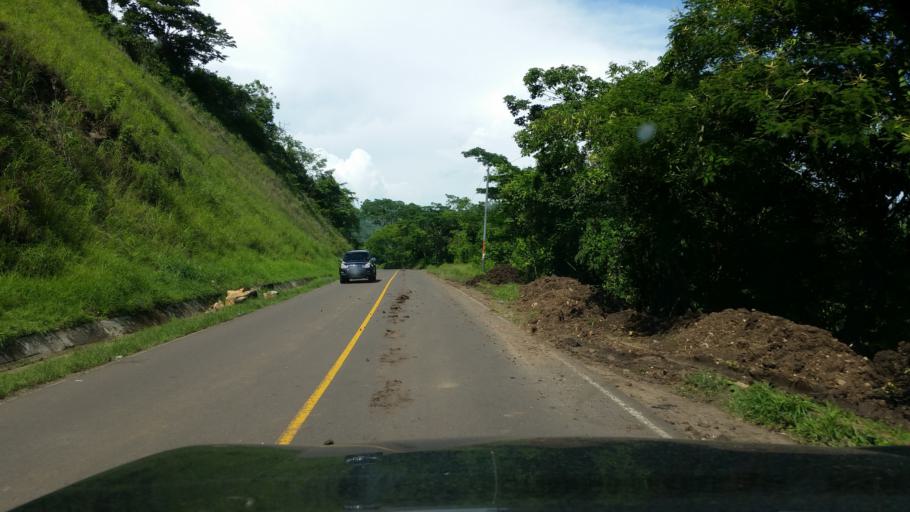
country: NI
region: Matagalpa
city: San Ramon
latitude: 13.0139
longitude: -85.7907
